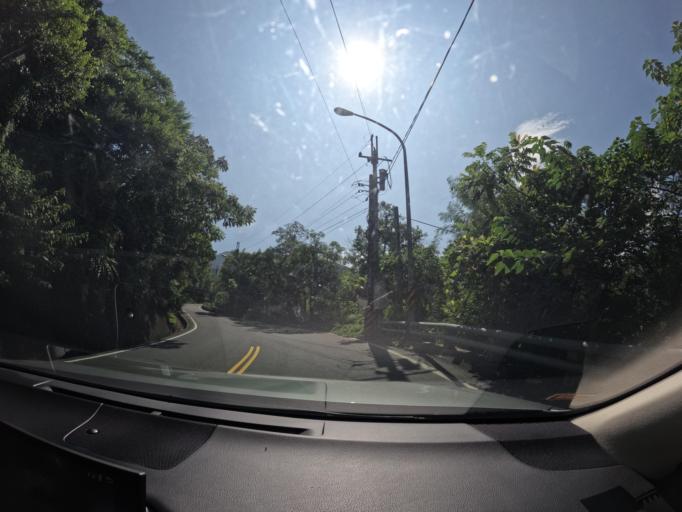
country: TW
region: Taiwan
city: Yujing
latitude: 23.1258
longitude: 120.7114
